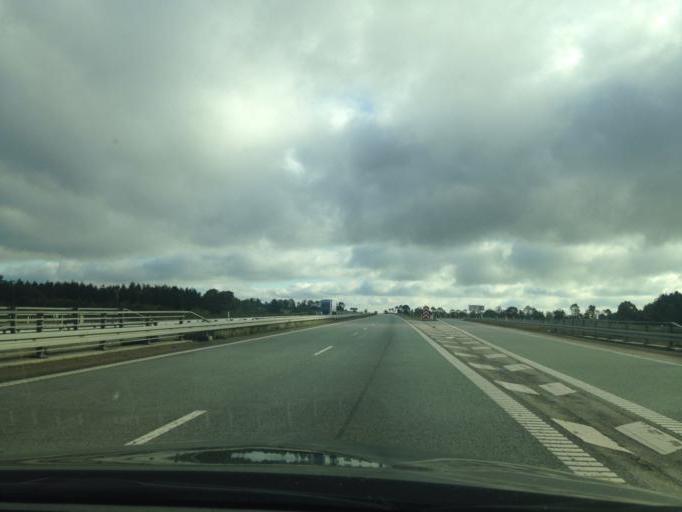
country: DK
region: South Denmark
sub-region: Vejle Kommune
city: Give
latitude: 55.8352
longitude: 9.3073
